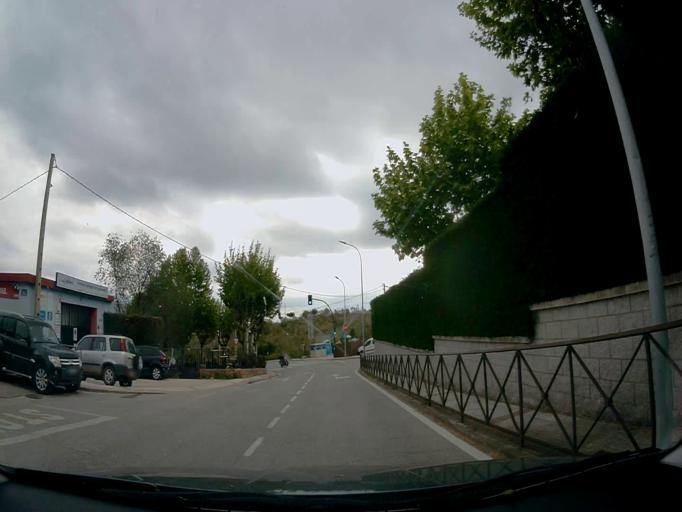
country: ES
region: Madrid
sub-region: Provincia de Madrid
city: Navalagamella
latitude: 40.4677
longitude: -4.1265
